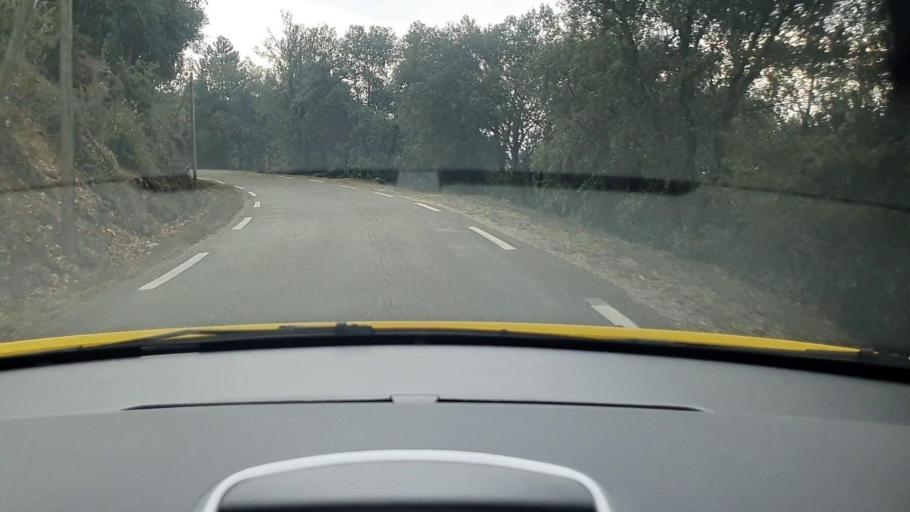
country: FR
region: Languedoc-Roussillon
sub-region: Departement du Gard
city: Besseges
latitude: 44.3447
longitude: 4.0389
